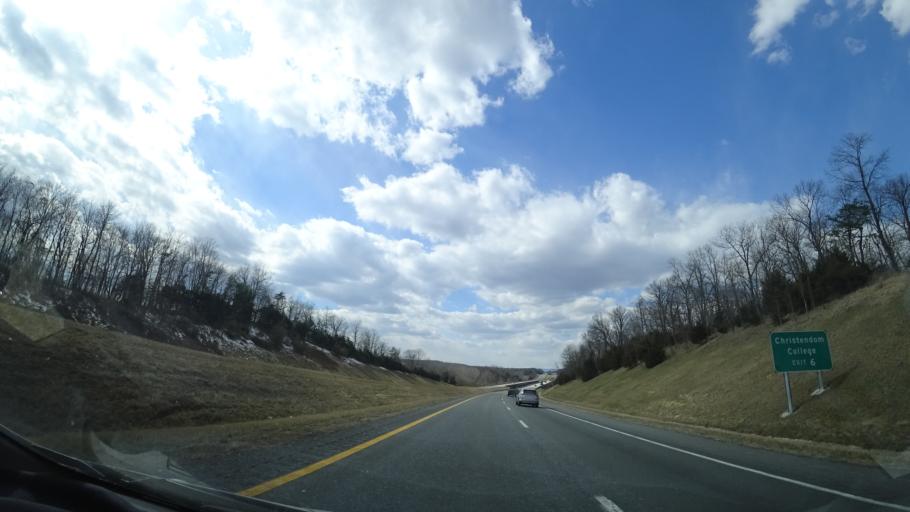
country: US
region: Virginia
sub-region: Warren County
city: Front Royal
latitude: 38.9530
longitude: -78.1802
